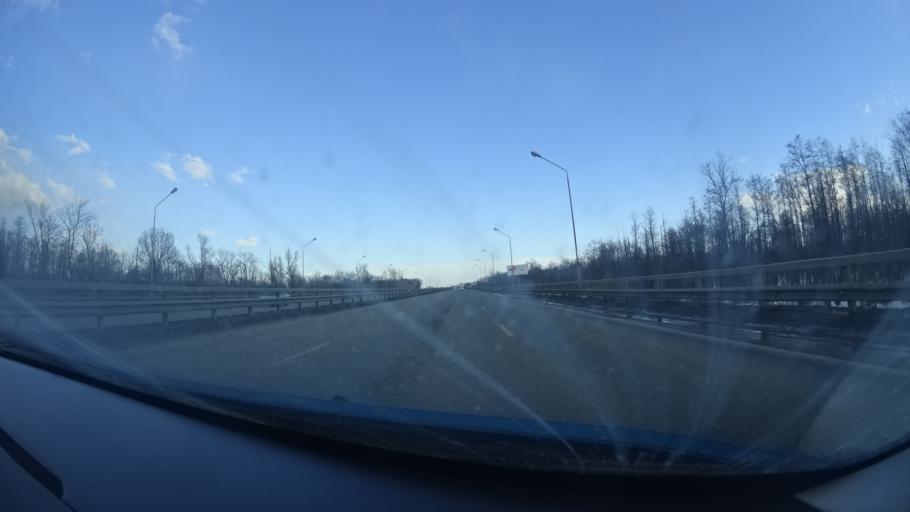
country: RU
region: Bashkortostan
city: Ufa
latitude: 54.6530
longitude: 55.9012
